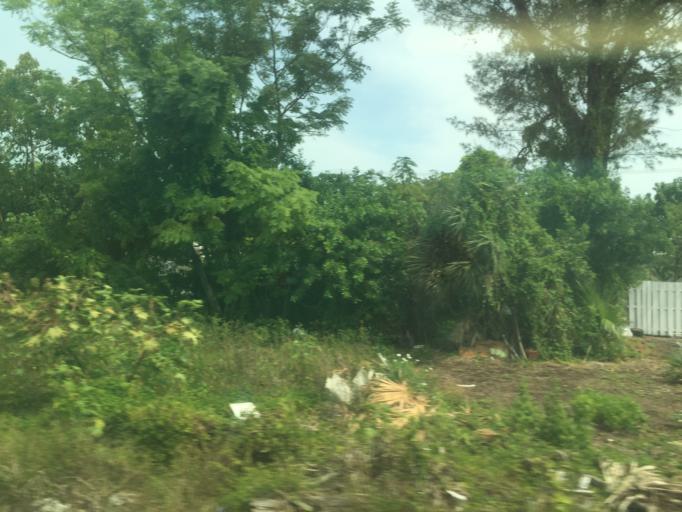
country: US
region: Florida
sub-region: Miami-Dade County
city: Opa-locka
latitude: 25.9016
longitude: -80.2496
